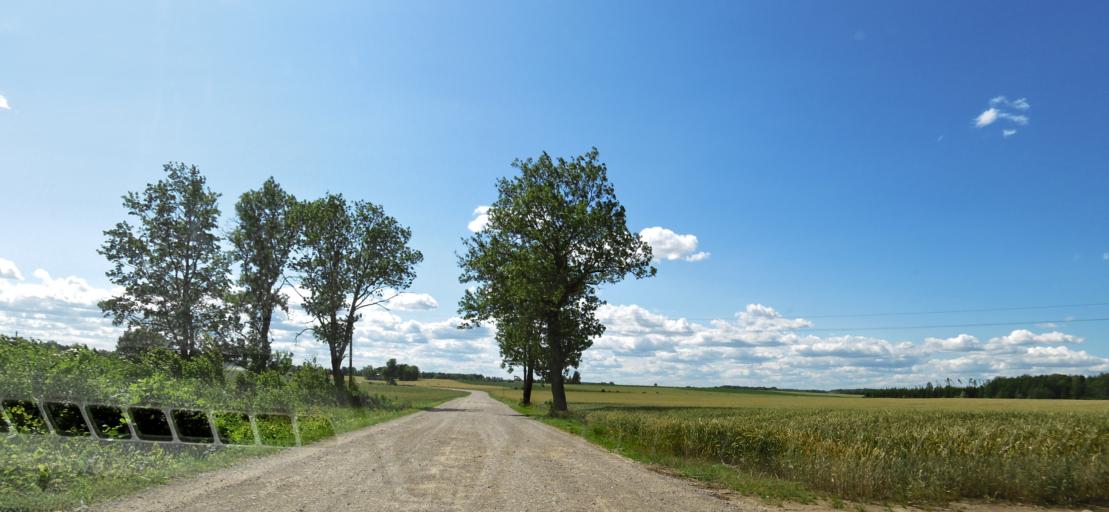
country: LV
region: Bauskas Rajons
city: Bauska
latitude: 56.2420
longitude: 24.2501
